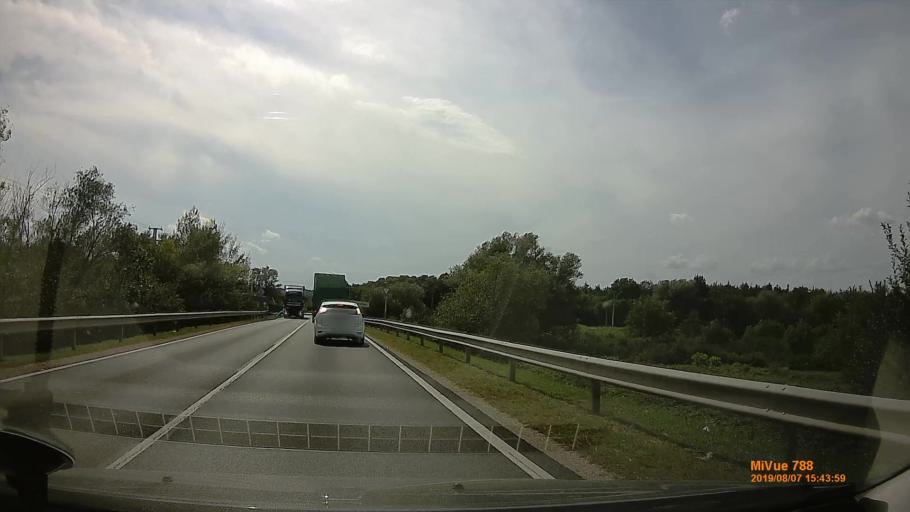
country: HU
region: Vas
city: Szombathely
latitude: 47.2090
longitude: 16.6194
